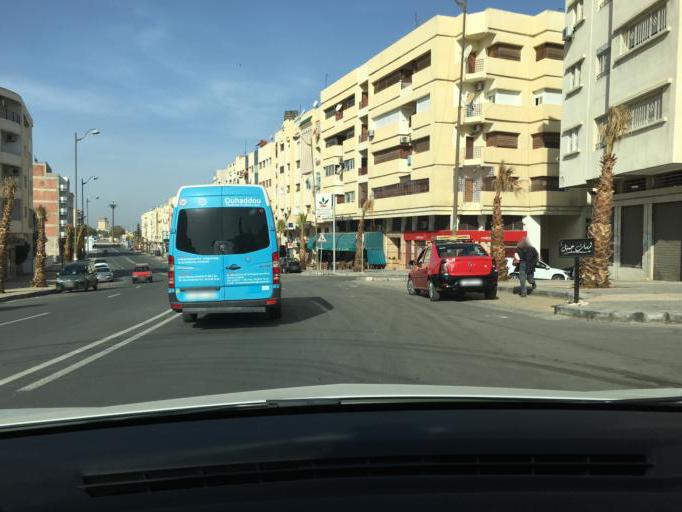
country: MA
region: Fes-Boulemane
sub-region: Fes
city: Fes
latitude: 34.0408
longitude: -5.0097
